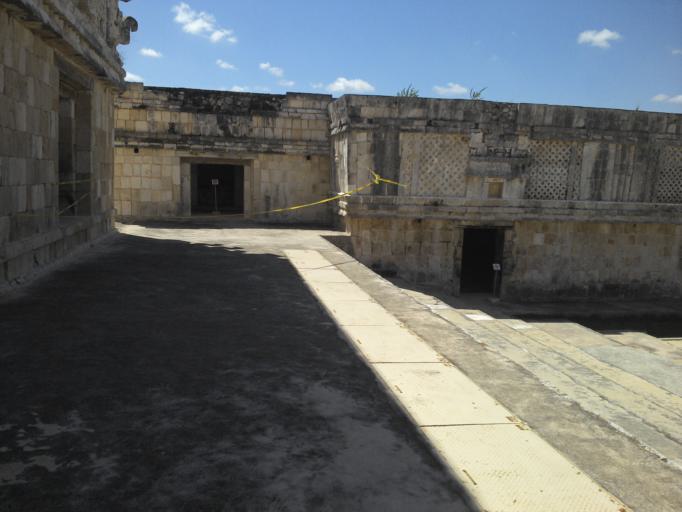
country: MX
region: Yucatan
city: Santa Elena
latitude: 20.3612
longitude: -89.7704
